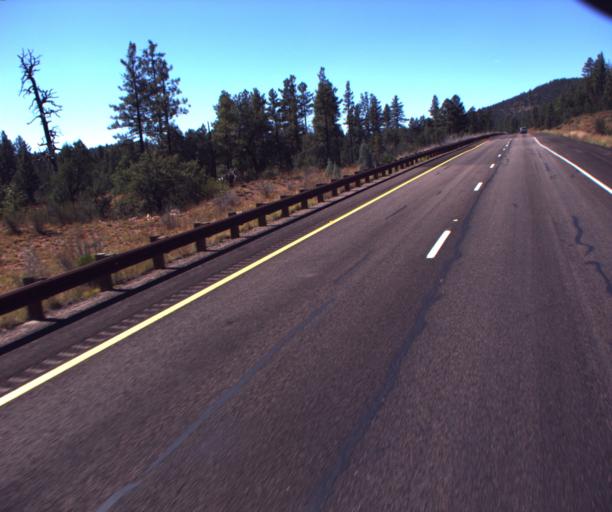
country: US
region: Arizona
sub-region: Gila County
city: Star Valley
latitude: 34.3287
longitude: -111.0965
